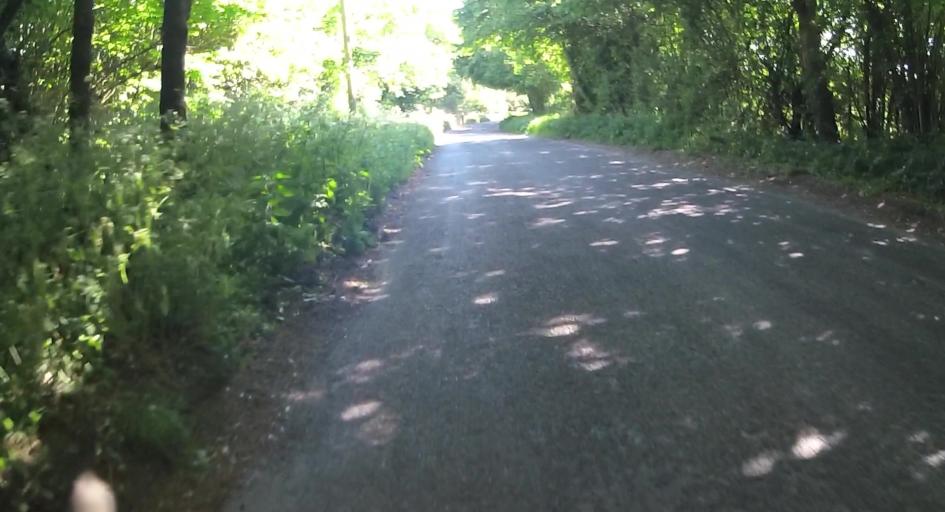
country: GB
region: England
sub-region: Hampshire
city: Old Basing
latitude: 51.2147
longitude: -1.0185
